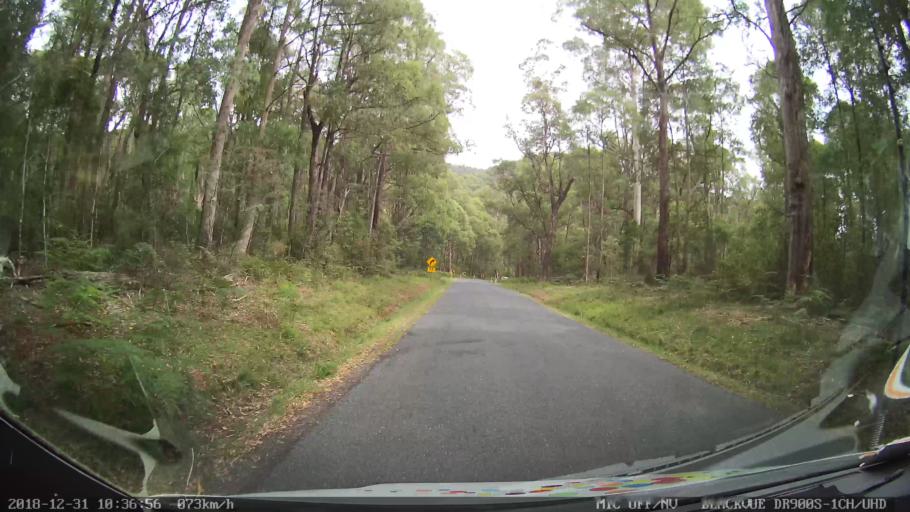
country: AU
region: New South Wales
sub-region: Snowy River
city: Jindabyne
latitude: -36.4208
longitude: 148.1701
